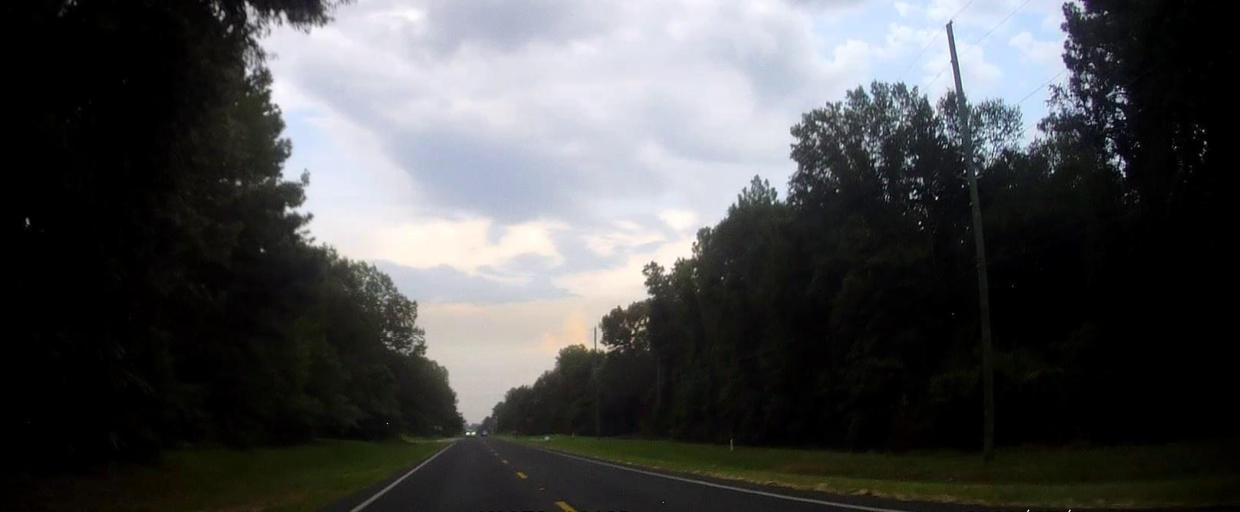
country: US
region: Georgia
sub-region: Laurens County
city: East Dublin
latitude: 32.5353
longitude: -82.8428
